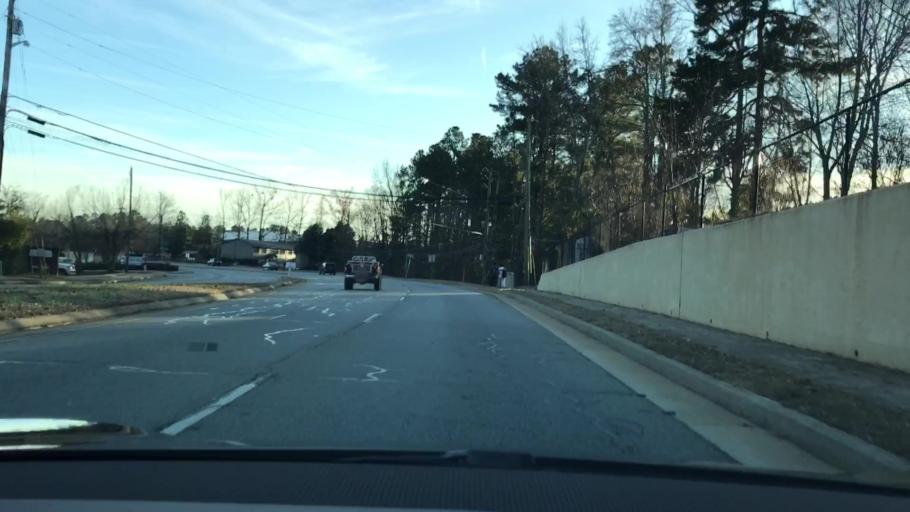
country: US
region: Georgia
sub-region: Gwinnett County
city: Buford
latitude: 34.0989
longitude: -84.0011
